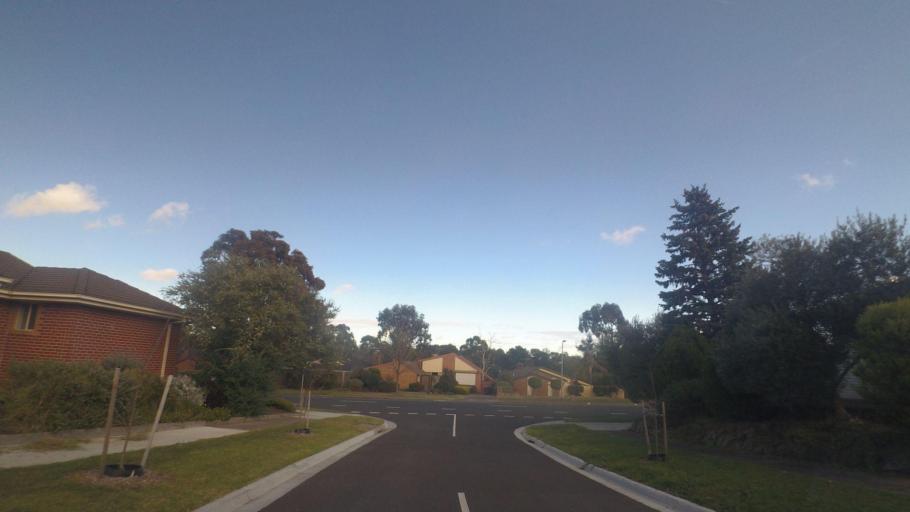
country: AU
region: Victoria
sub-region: Knox
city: Scoresby
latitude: -37.9142
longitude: 145.2437
